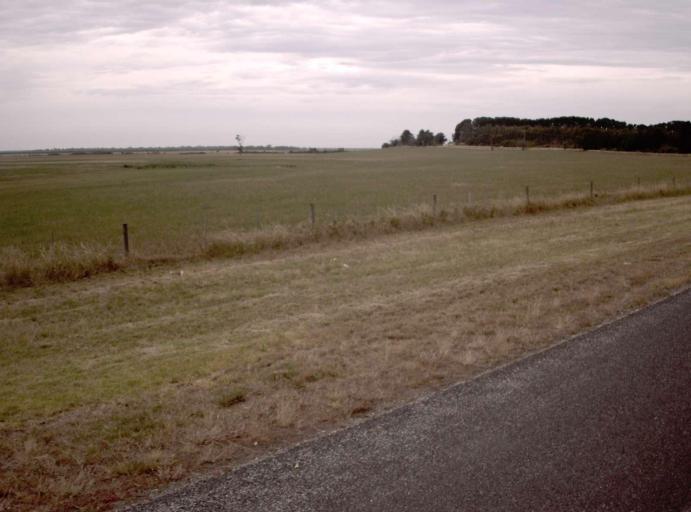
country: AU
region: Victoria
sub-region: Wellington
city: Sale
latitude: -38.1959
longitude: 147.2917
